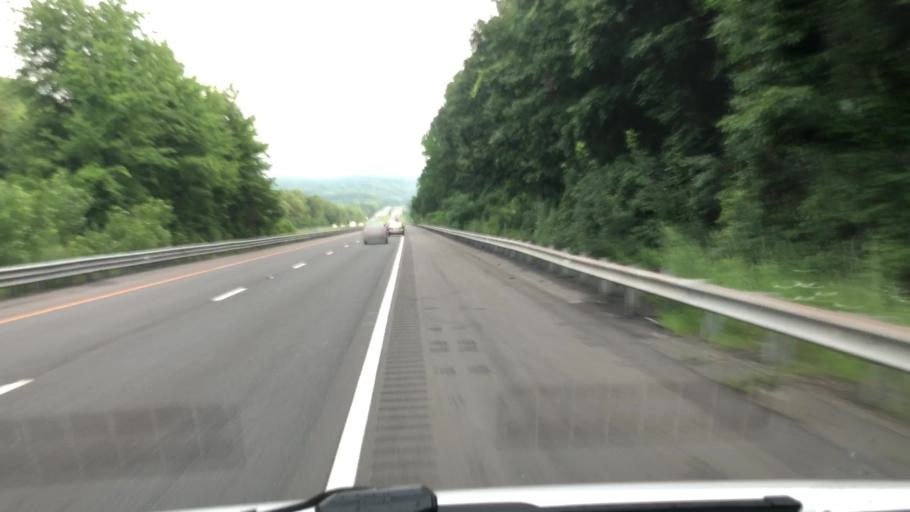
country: US
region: Massachusetts
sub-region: Franklin County
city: South Deerfield
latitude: 42.5106
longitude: -72.6216
